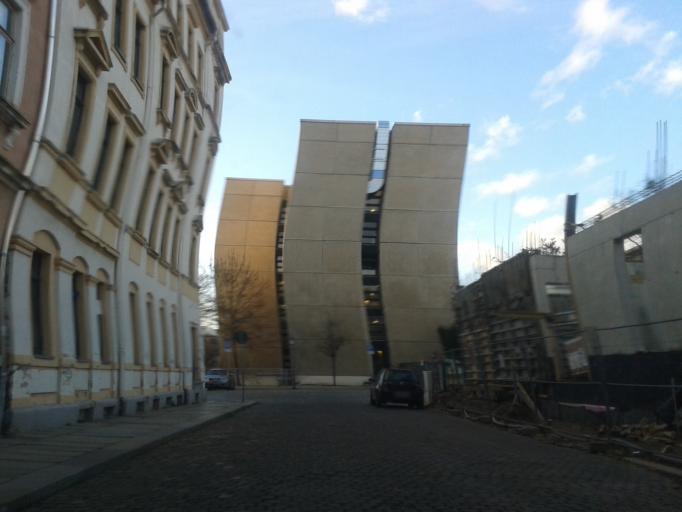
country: DE
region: Saxony
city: Dresden
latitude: 51.0578
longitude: 13.7201
